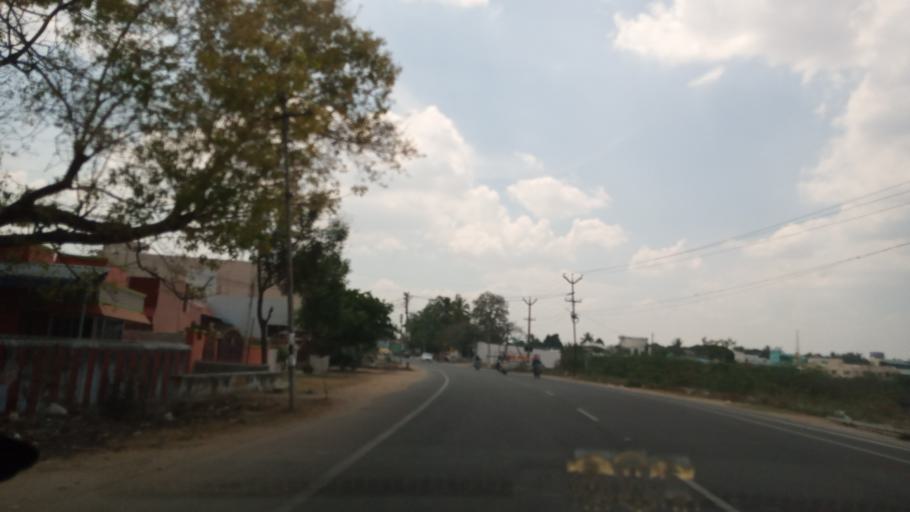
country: IN
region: Tamil Nadu
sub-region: Vellore
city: Walajapet
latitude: 12.9232
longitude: 79.3749
